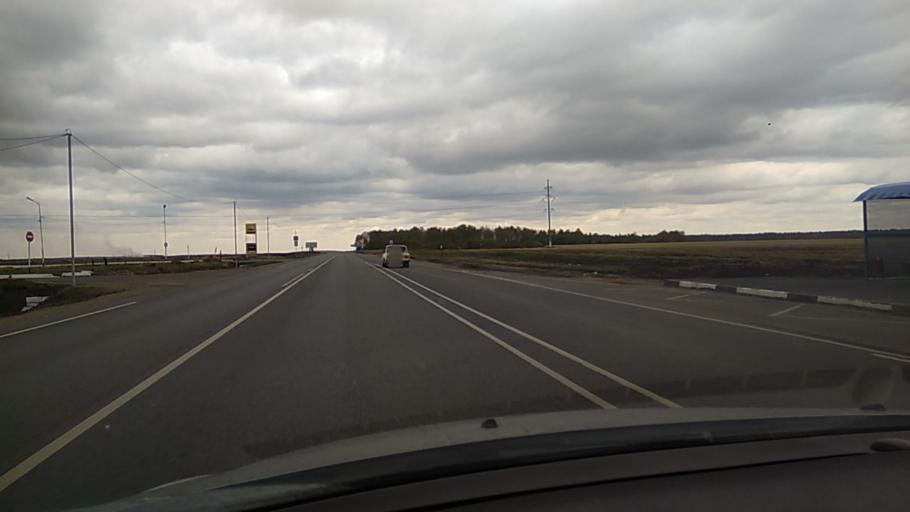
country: RU
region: Kurgan
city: Kataysk
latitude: 56.3099
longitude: 62.6105
